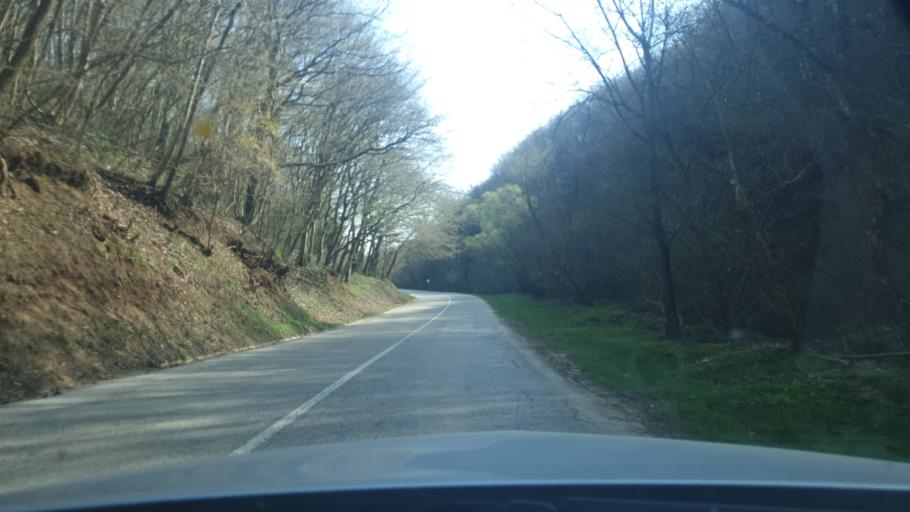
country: RS
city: Vrdnik
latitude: 45.1428
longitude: 19.7720
